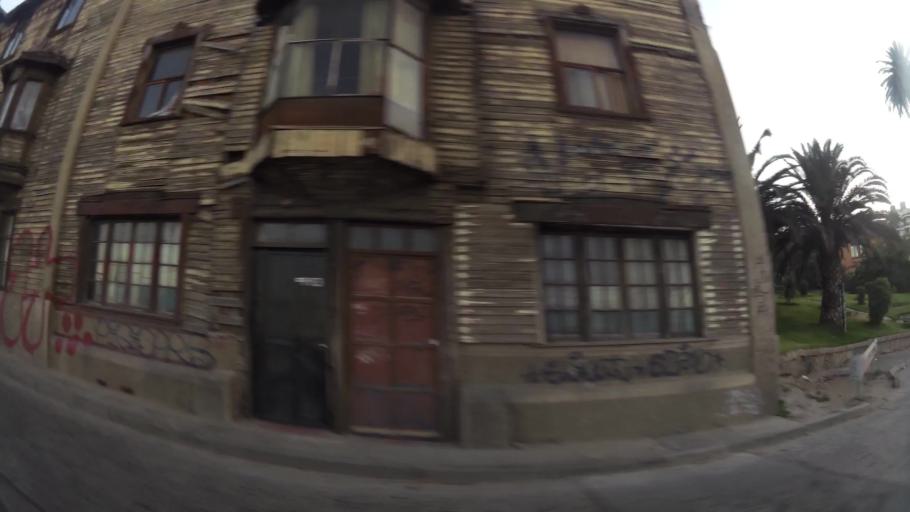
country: CL
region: Valparaiso
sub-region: Provincia de Valparaiso
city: Vina del Mar
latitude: -33.0280
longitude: -71.5767
